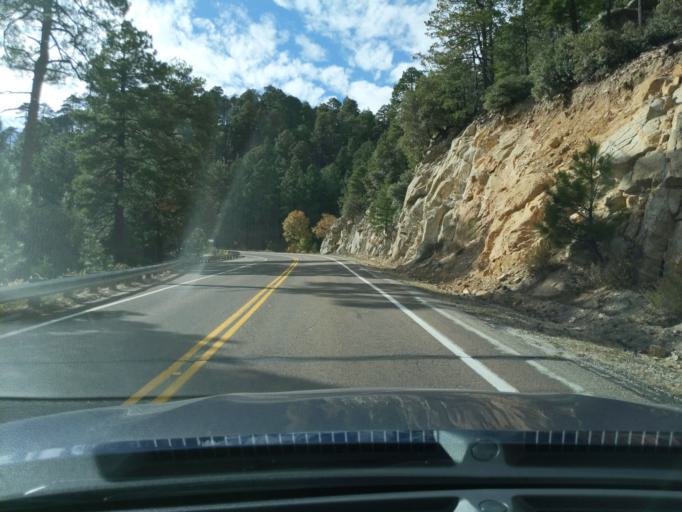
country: US
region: Arizona
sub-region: Pima County
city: Tanque Verde
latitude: 32.4111
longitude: -110.7217
